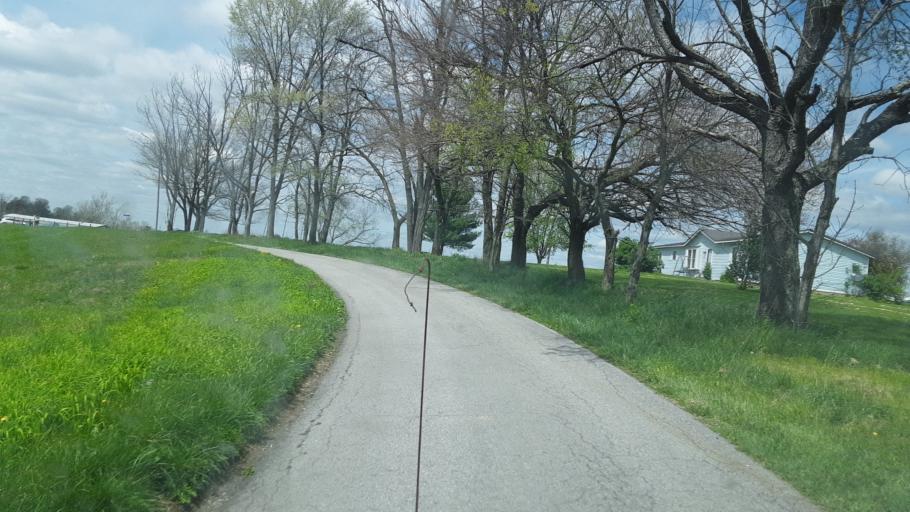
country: US
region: Kentucky
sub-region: Gallatin County
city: Warsaw
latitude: 38.6748
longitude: -84.8128
